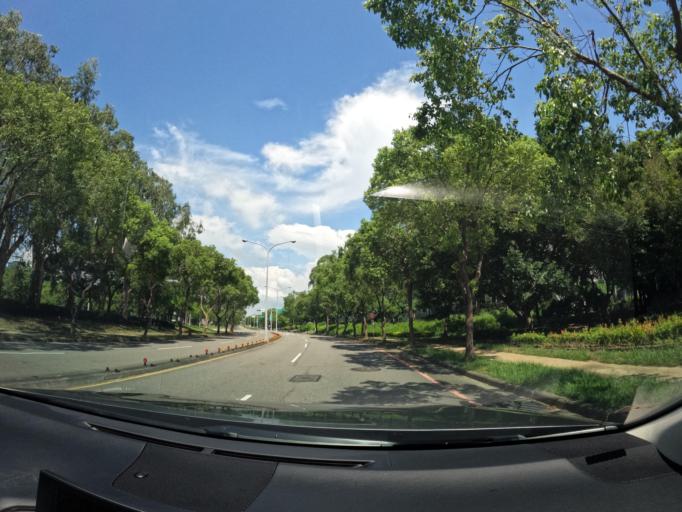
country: TW
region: Taiwan
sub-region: Hsinchu
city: Hsinchu
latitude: 24.7065
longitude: 120.9184
